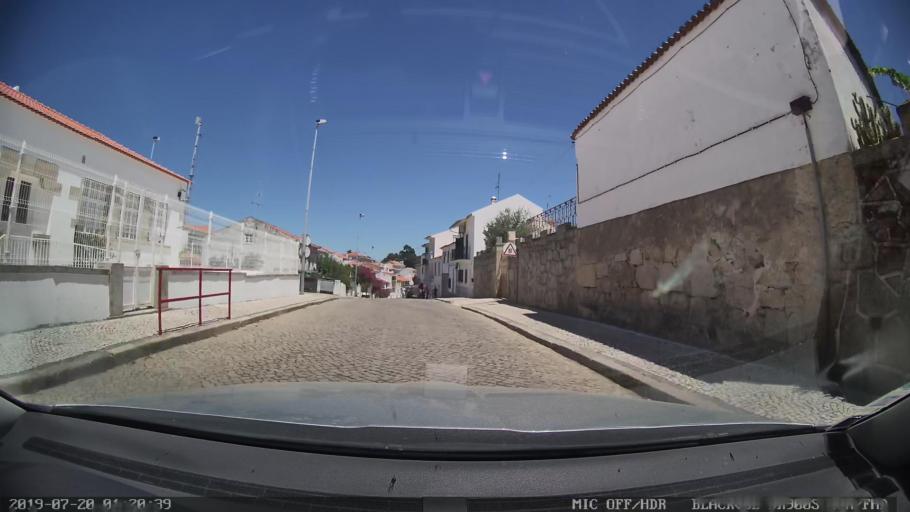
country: PT
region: Castelo Branco
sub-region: Idanha-A-Nova
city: Idanha-a-Nova
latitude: 39.9240
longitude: -7.2388
